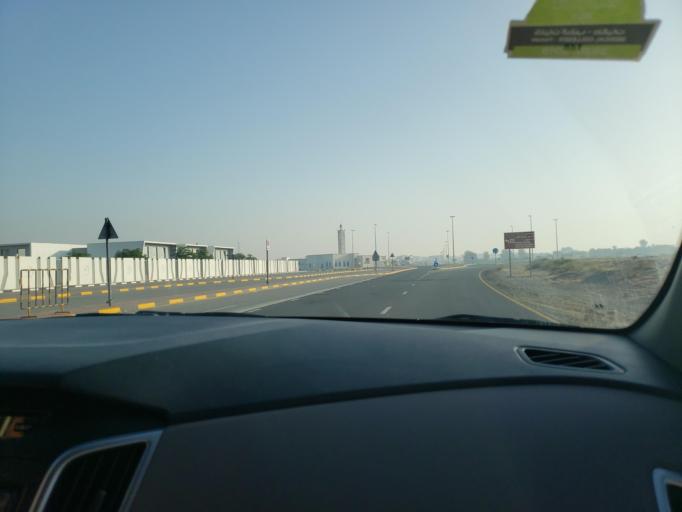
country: AE
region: Umm al Qaywayn
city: Umm al Qaywayn
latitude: 25.4678
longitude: 55.6128
